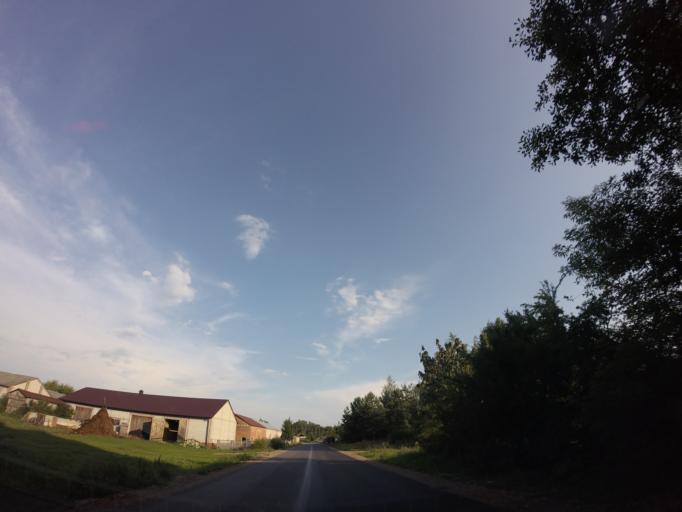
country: PL
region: Lublin Voivodeship
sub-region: Powiat pulawski
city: Kurow
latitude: 51.4173
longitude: 22.2274
